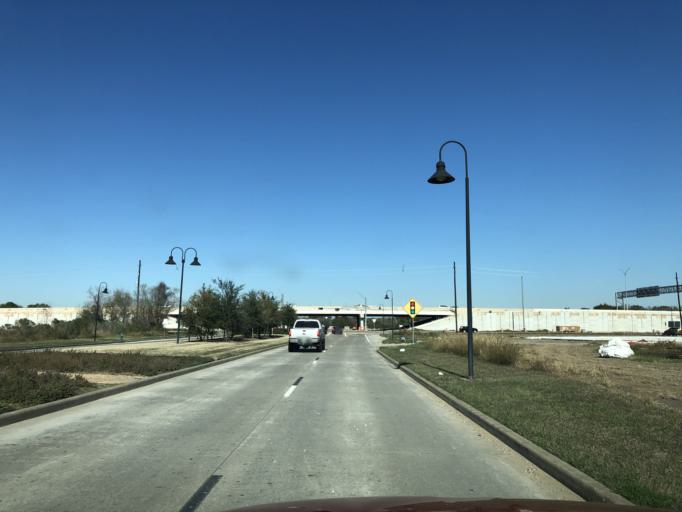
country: US
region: Texas
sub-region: Fort Bend County
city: Fresno
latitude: 29.5948
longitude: -95.4006
